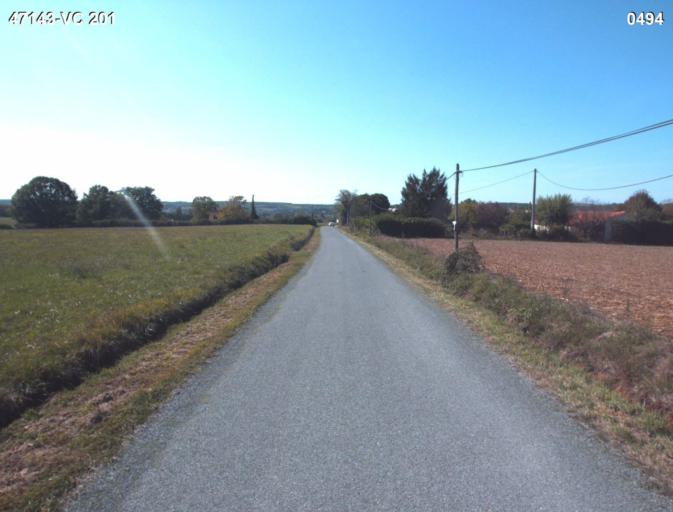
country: FR
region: Aquitaine
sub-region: Departement du Lot-et-Garonne
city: Vianne
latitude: 44.1829
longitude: 0.3142
